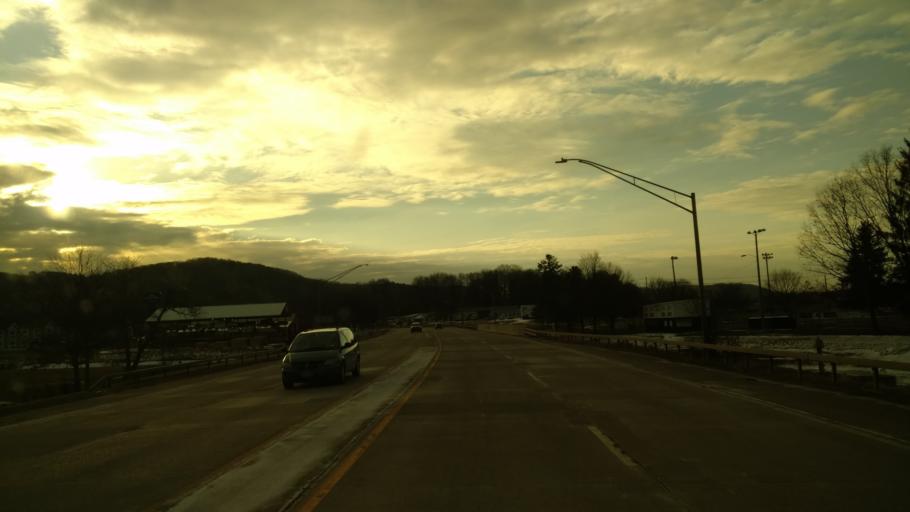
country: US
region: New York
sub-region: Allegany County
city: Wellsville
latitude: 42.1178
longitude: -77.9447
